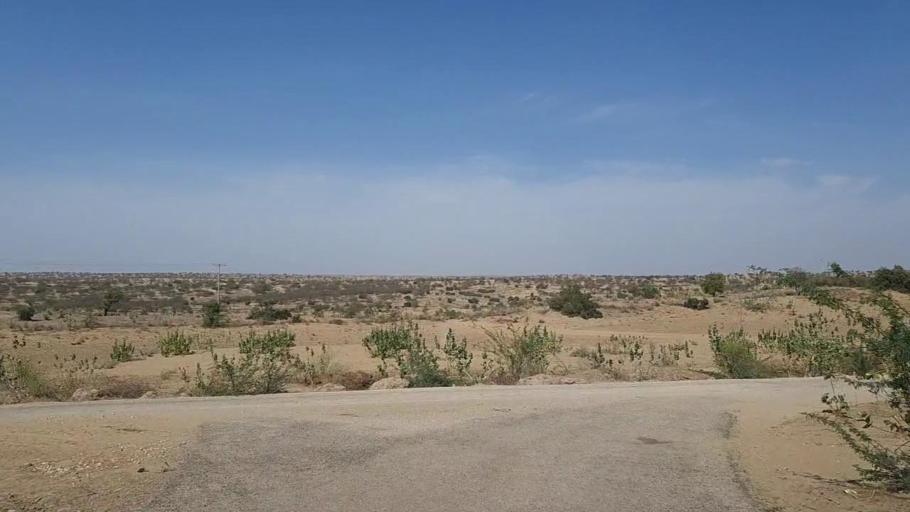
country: PK
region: Sindh
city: Mithi
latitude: 24.8596
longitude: 69.6692
